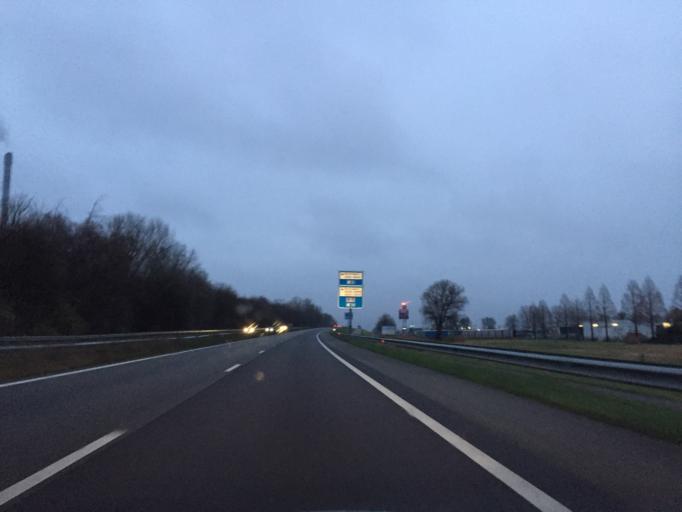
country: NL
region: North Brabant
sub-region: Roosendaal
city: Roosendaal
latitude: 51.5458
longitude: 4.4440
